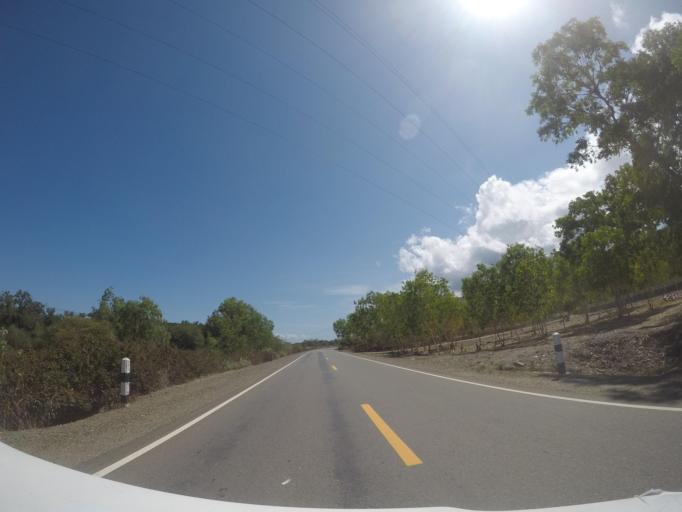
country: ID
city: Metinaro
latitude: -8.5019
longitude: 125.8131
